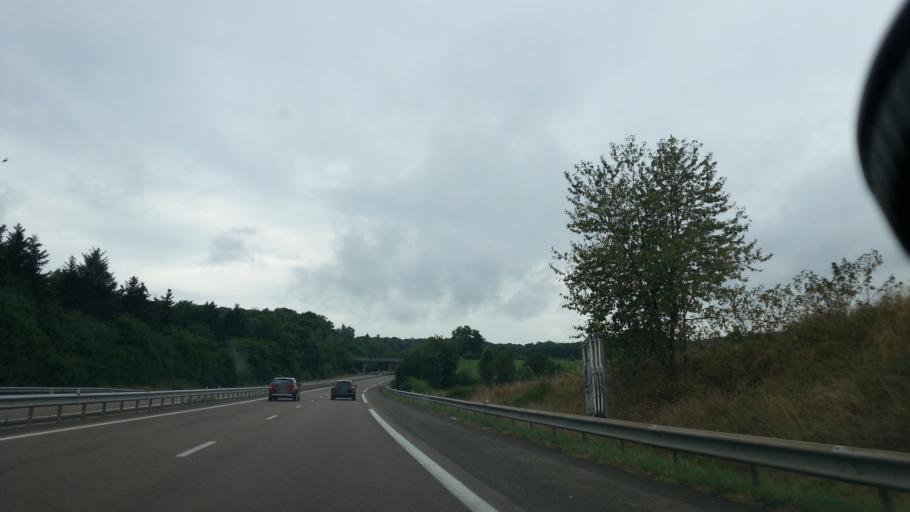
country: FR
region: Franche-Comte
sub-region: Departement du Jura
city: Orchamps
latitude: 47.1551
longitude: 5.6065
